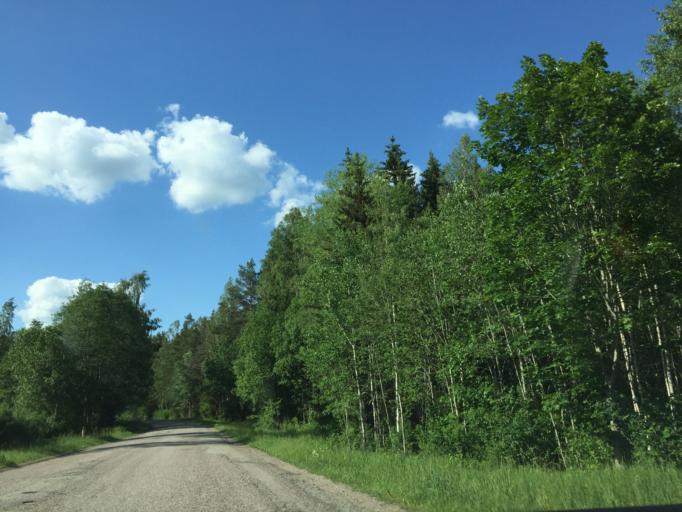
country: LV
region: Jaunpils
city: Jaunpils
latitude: 56.8661
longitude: 23.0077
